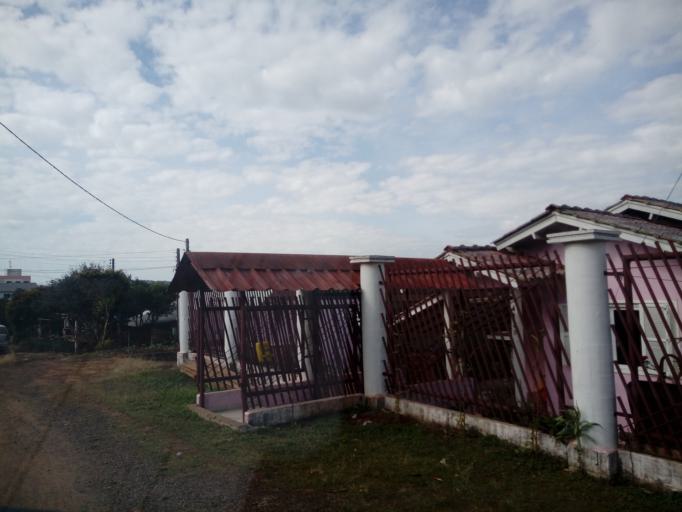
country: BR
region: Santa Catarina
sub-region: Chapeco
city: Chapeco
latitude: -27.1225
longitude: -52.6236
